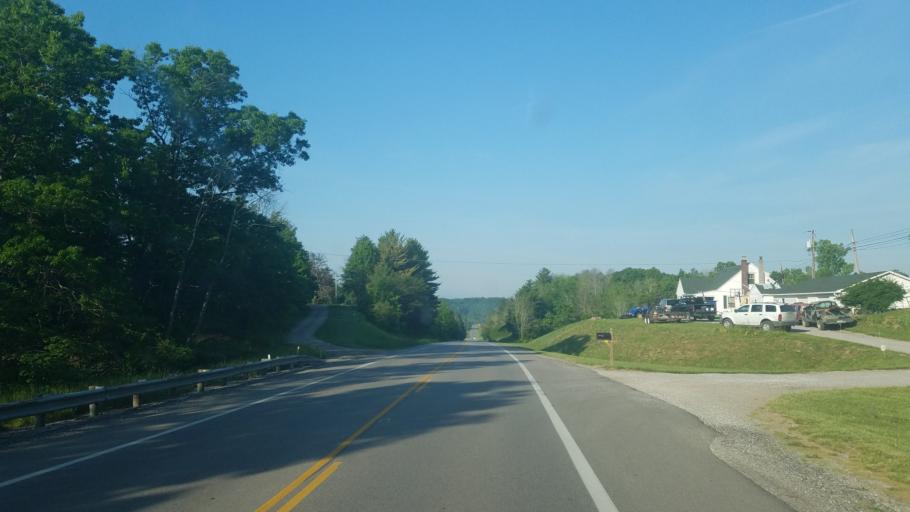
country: US
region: West Virginia
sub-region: Mason County
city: New Haven
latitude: 39.1311
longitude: -81.8732
